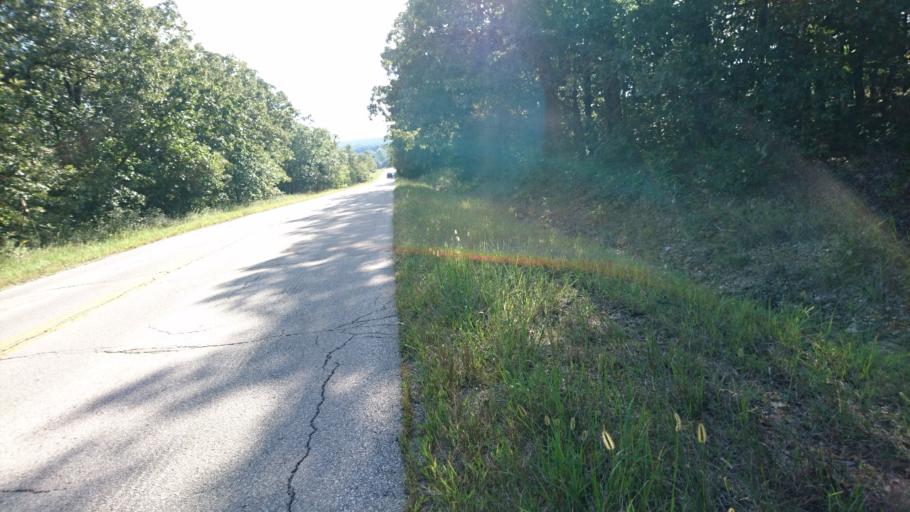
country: US
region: Missouri
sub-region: Crawford County
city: Cuba
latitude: 38.1115
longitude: -91.3310
